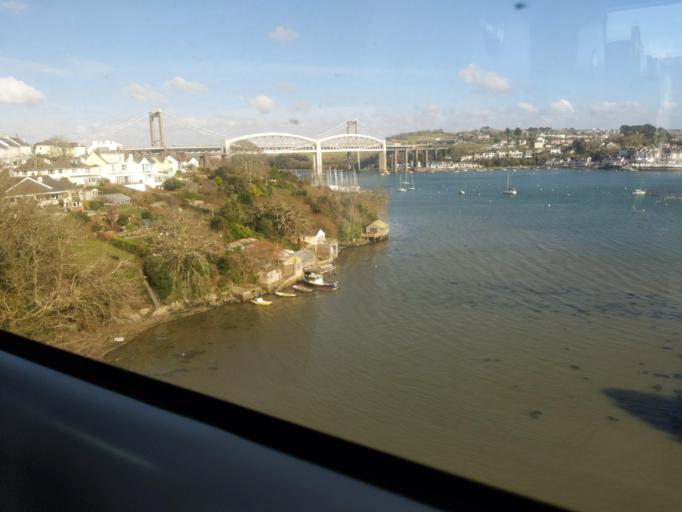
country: GB
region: England
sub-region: Cornwall
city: Saltash
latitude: 50.4044
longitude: -4.2116
